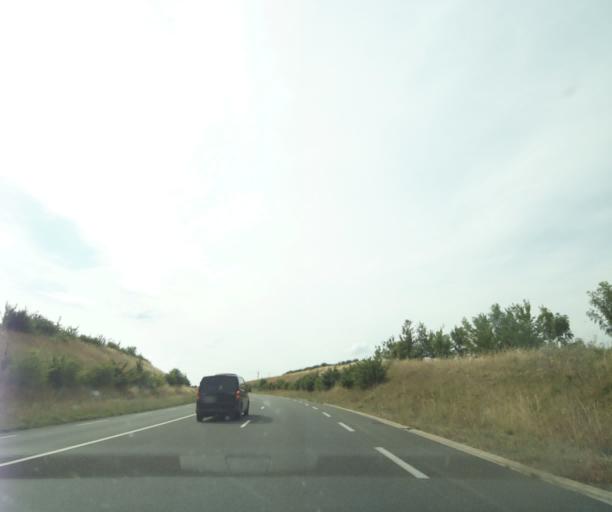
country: FR
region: Pays de la Loire
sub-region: Departement de la Sarthe
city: Luceau
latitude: 47.7116
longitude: 0.4092
